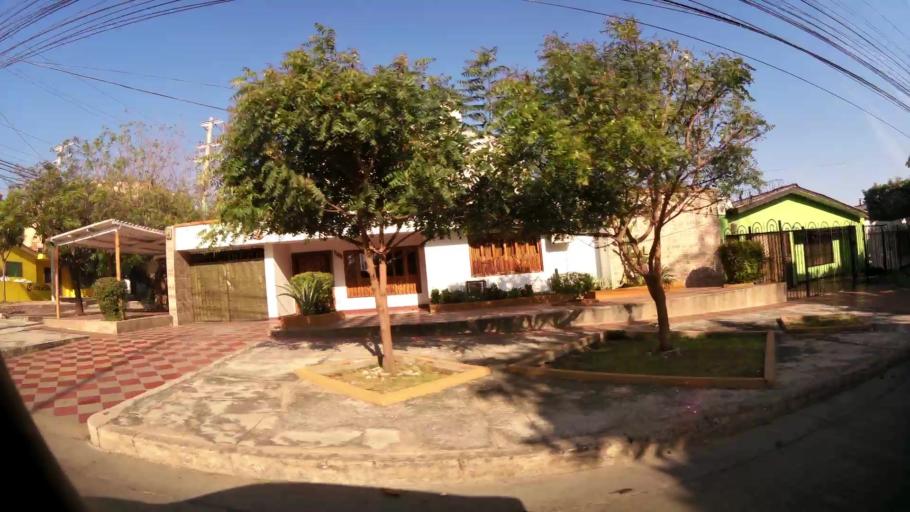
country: CO
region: Atlantico
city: Barranquilla
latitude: 11.0091
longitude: -74.7959
